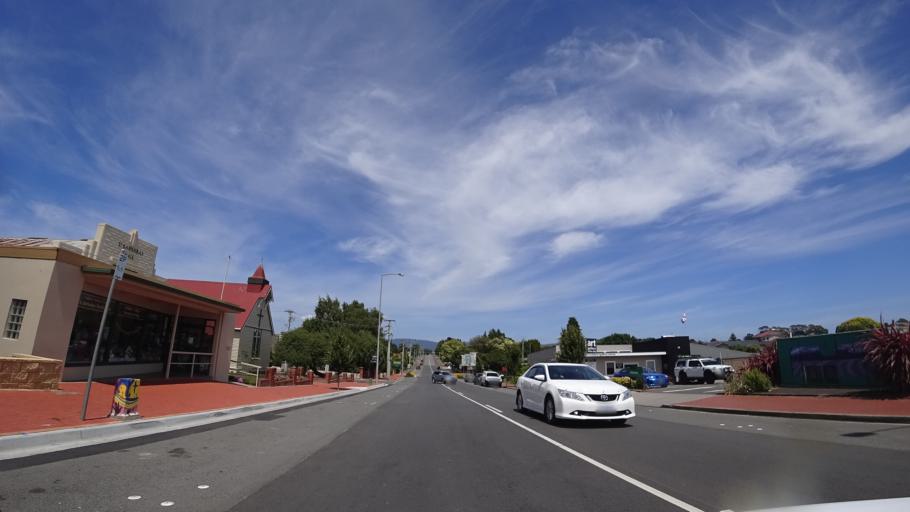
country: AU
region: Tasmania
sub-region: Dorset
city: Scottsdale
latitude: -41.1621
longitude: 147.5149
